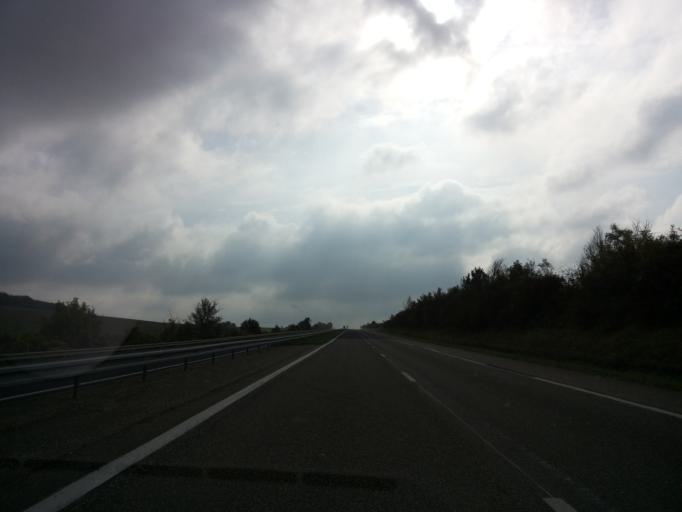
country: FR
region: Lorraine
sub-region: Departement de la Moselle
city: Solgne
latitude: 48.9413
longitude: 6.3228
